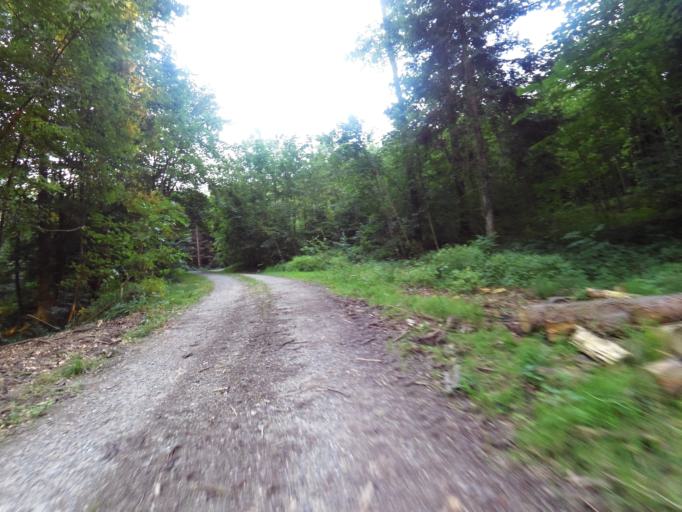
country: CH
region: Thurgau
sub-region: Weinfelden District
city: Wigoltingen
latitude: 47.5733
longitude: 9.0310
